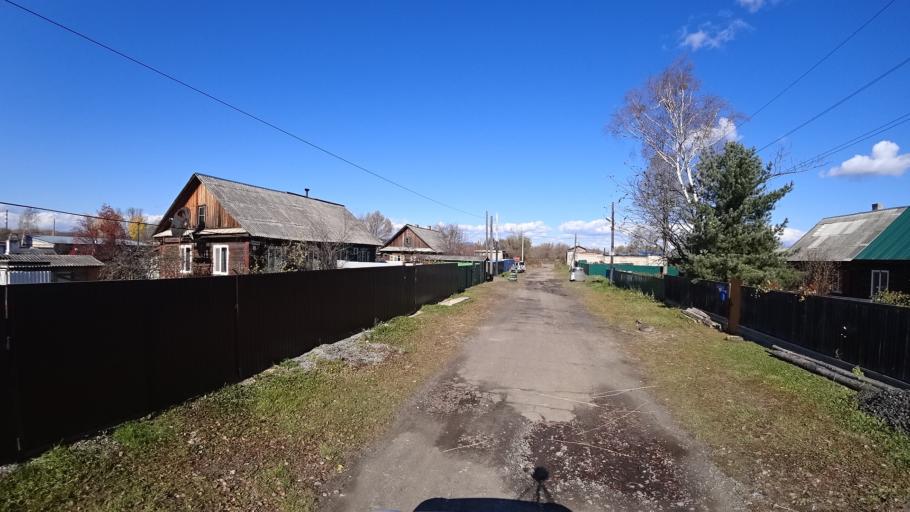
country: RU
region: Khabarovsk Krai
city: Amursk
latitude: 50.1006
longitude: 136.4985
